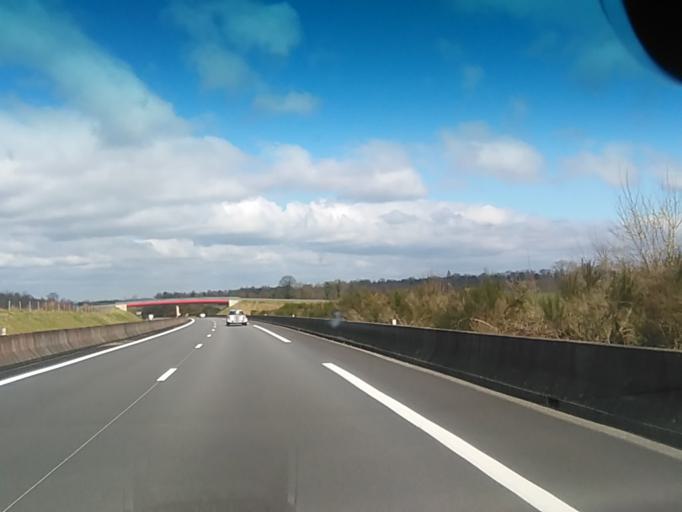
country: FR
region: Lower Normandy
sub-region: Departement du Calvados
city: Orbec
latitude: 49.0125
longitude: 0.4461
